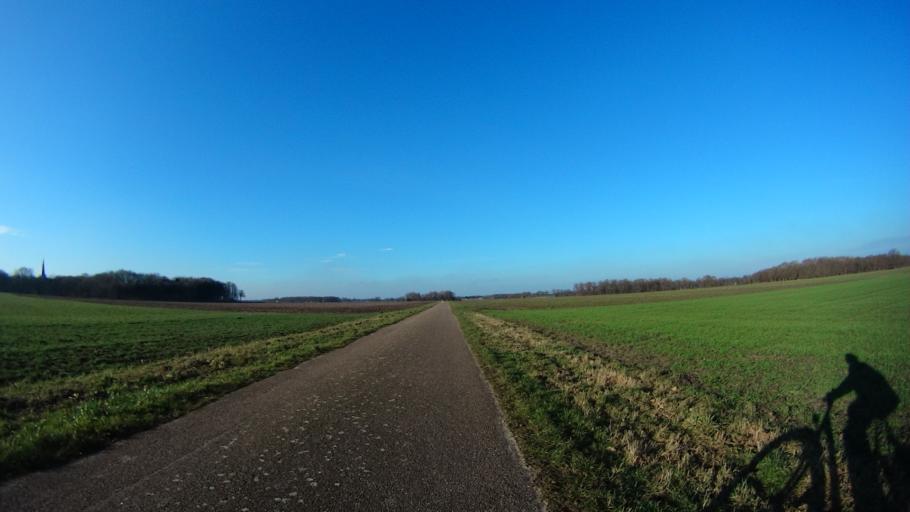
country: NL
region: Drenthe
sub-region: Gemeente Coevorden
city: Sleen
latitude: 52.7752
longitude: 6.8118
